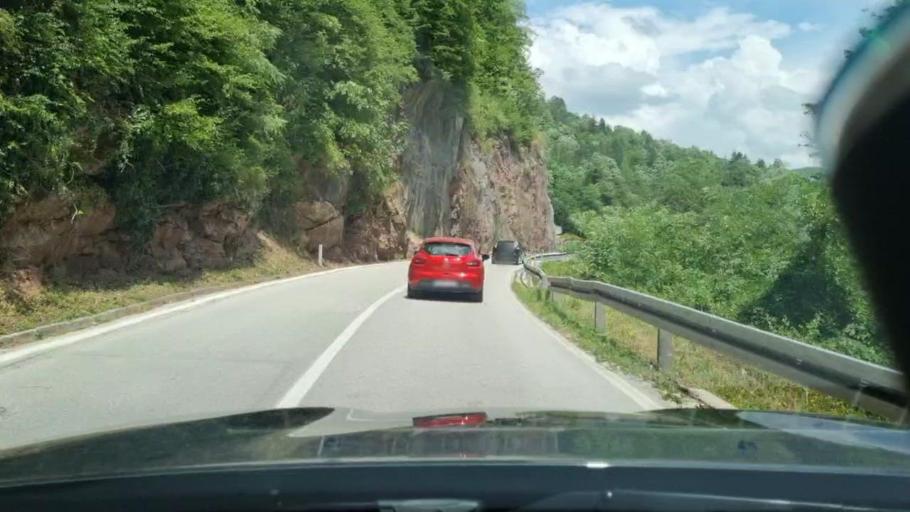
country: BA
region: Federation of Bosnia and Herzegovina
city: Prozor
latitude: 43.7493
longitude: 17.6756
